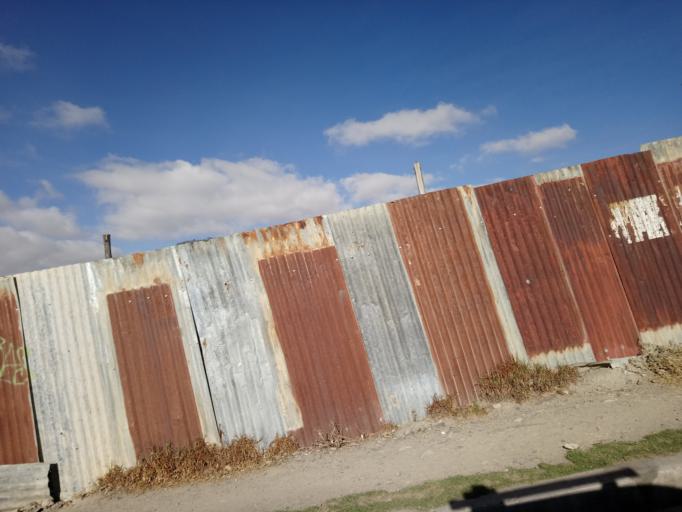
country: BO
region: La Paz
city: La Paz
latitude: -16.5128
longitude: -68.1144
